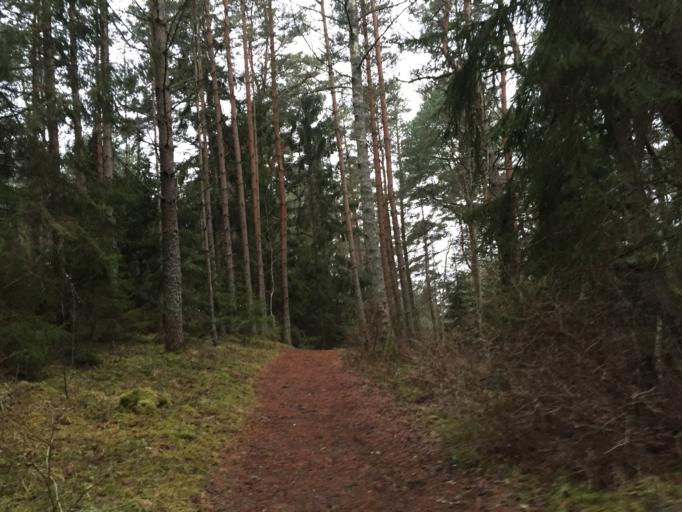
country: EE
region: Saare
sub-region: Kuressaare linn
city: Kuressaare
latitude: 58.5923
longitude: 22.5052
